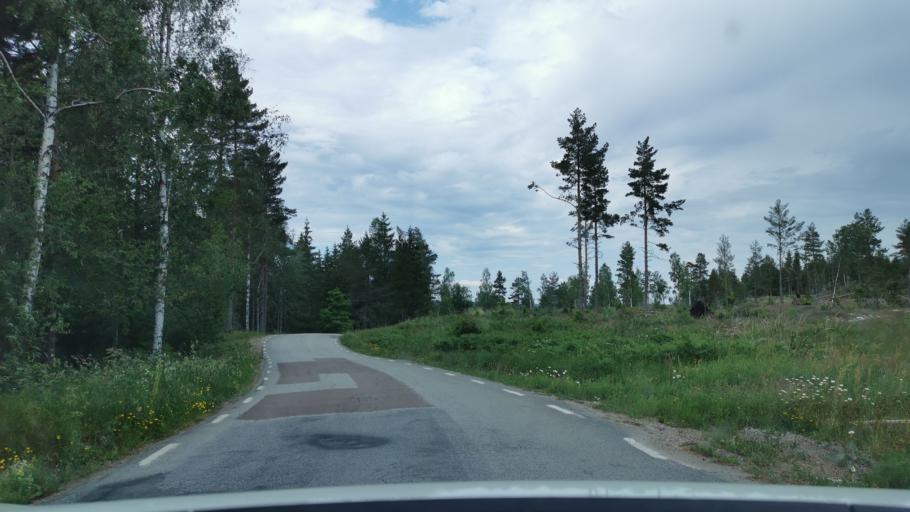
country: SE
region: Vaestra Goetaland
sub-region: Bengtsfors Kommun
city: Dals Langed
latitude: 58.8793
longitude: 12.4049
